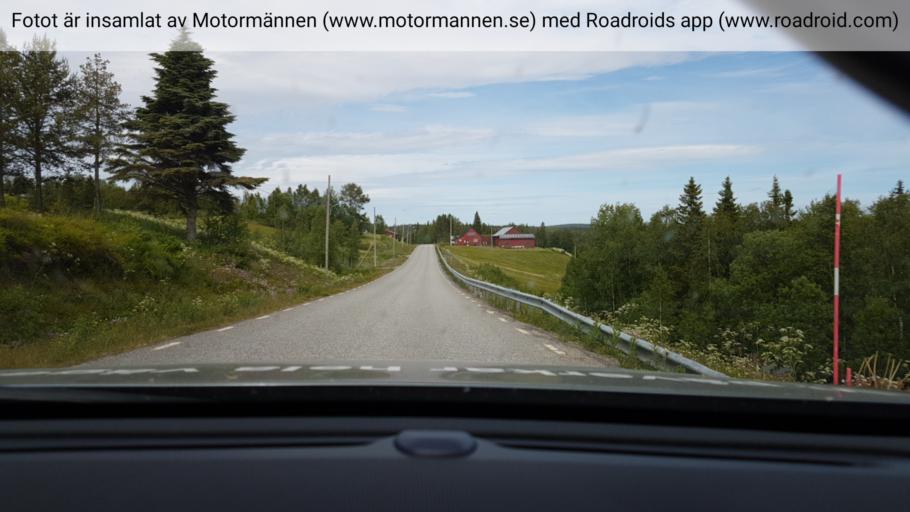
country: SE
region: Vaesterbotten
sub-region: Vilhelmina Kommun
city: Sjoberg
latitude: 65.1406
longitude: 16.2935
